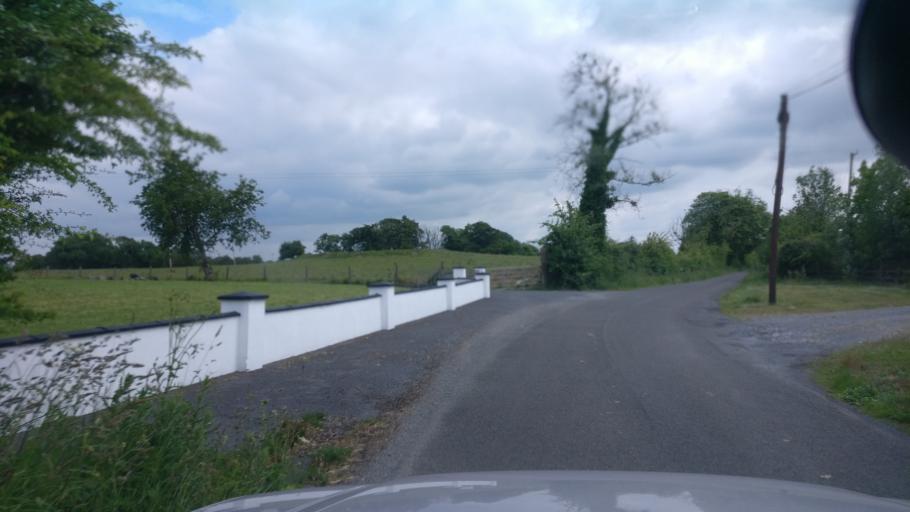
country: IE
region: Connaught
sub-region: County Galway
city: Ballinasloe
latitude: 53.2855
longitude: -8.3402
